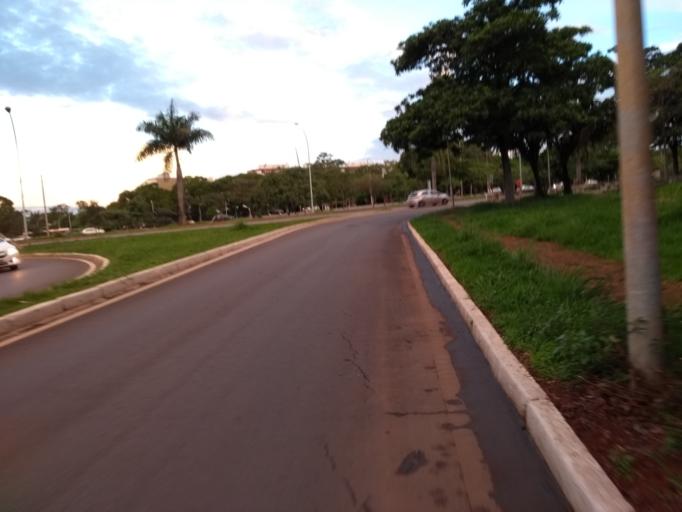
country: BR
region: Federal District
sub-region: Brasilia
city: Brasilia
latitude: -15.7402
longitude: -47.8923
